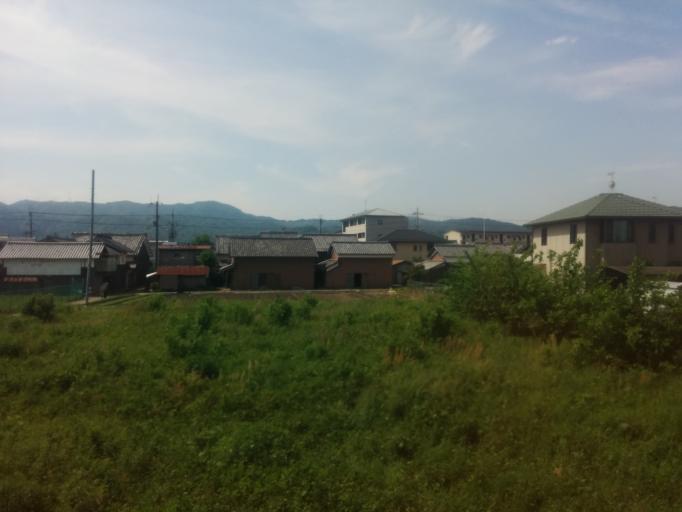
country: JP
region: Kyoto
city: Kameoka
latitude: 35.0104
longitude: 135.5963
